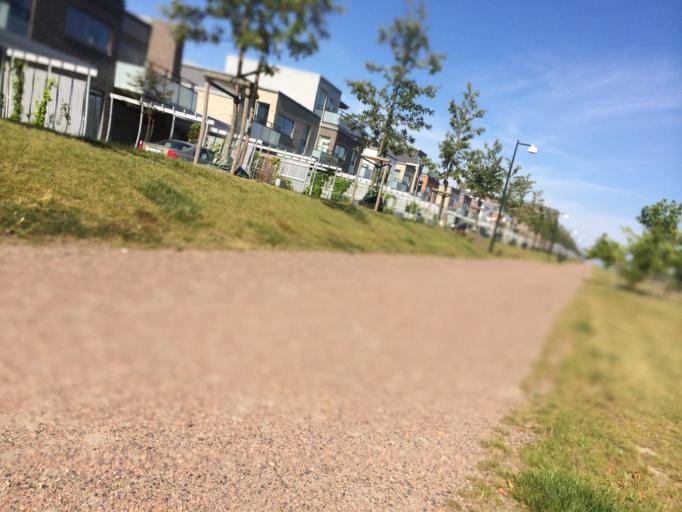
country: SE
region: Skane
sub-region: Malmo
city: Bunkeflostrand
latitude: 55.5916
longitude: 12.9348
